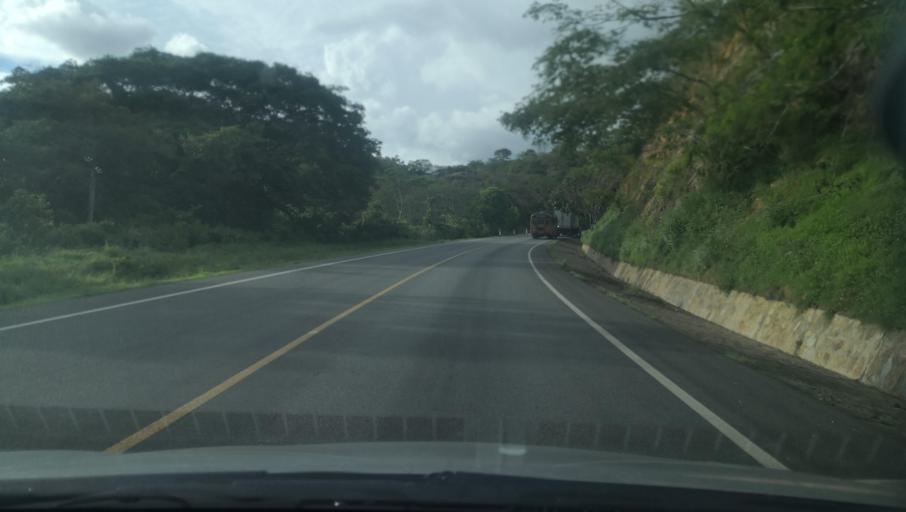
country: NI
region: Nueva Segovia
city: Ocotal
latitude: 13.6849
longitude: -86.4889
